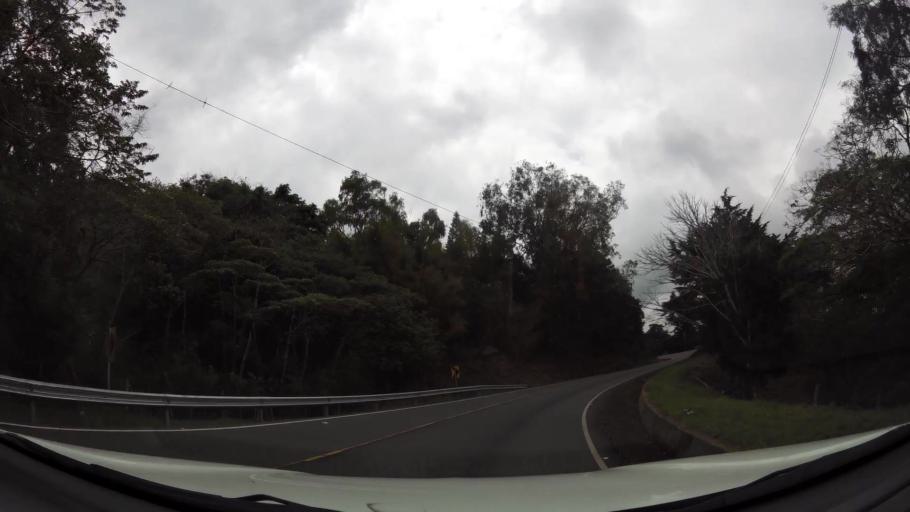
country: NI
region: Matagalpa
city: Matagalpa
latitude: 12.9803
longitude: -85.9220
